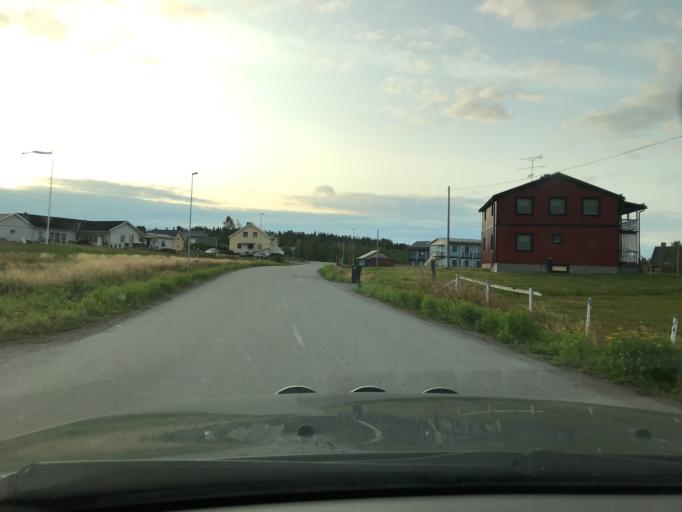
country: SE
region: Norrbotten
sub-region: Gallivare Kommun
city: Malmberget
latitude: 67.6459
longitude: 21.0508
